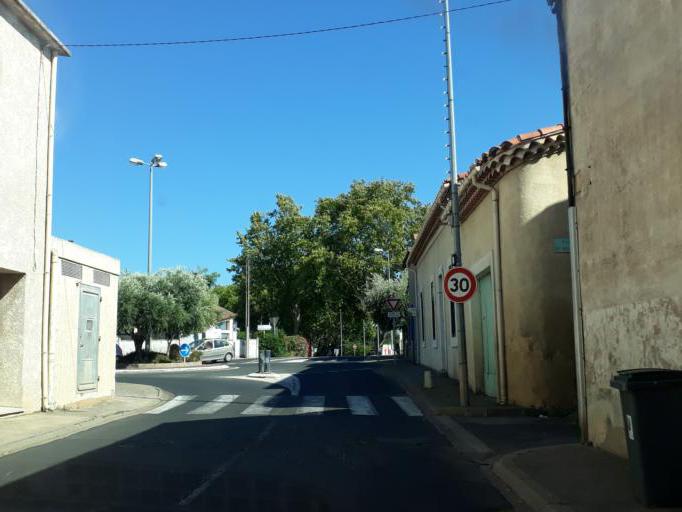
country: FR
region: Languedoc-Roussillon
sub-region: Departement de l'Herault
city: Florensac
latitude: 43.3806
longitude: 3.4684
